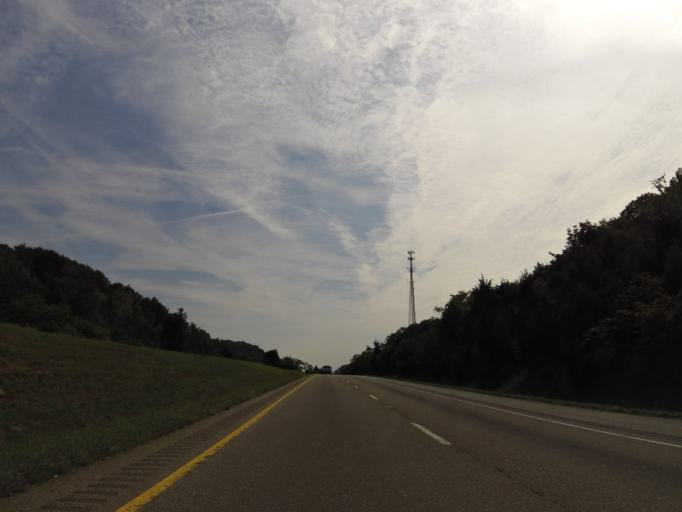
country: US
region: Tennessee
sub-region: Hamblen County
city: Morristown
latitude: 36.2000
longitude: -83.1296
